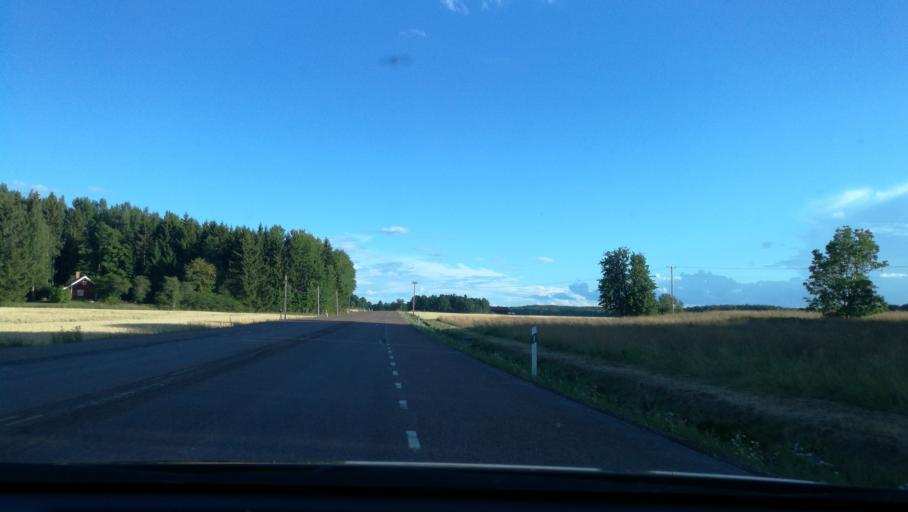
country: SE
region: Vaestmanland
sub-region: Kopings Kommun
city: Koping
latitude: 59.4748
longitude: 15.9905
